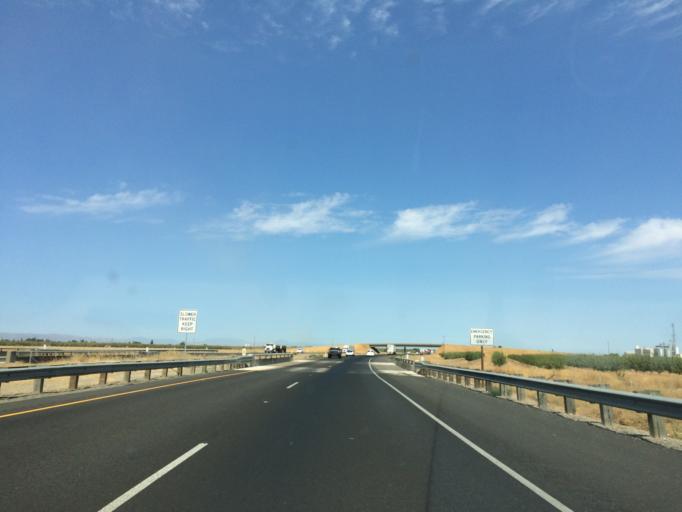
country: US
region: California
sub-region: Colusa County
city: Arbuckle
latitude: 38.9516
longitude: -122.0156
